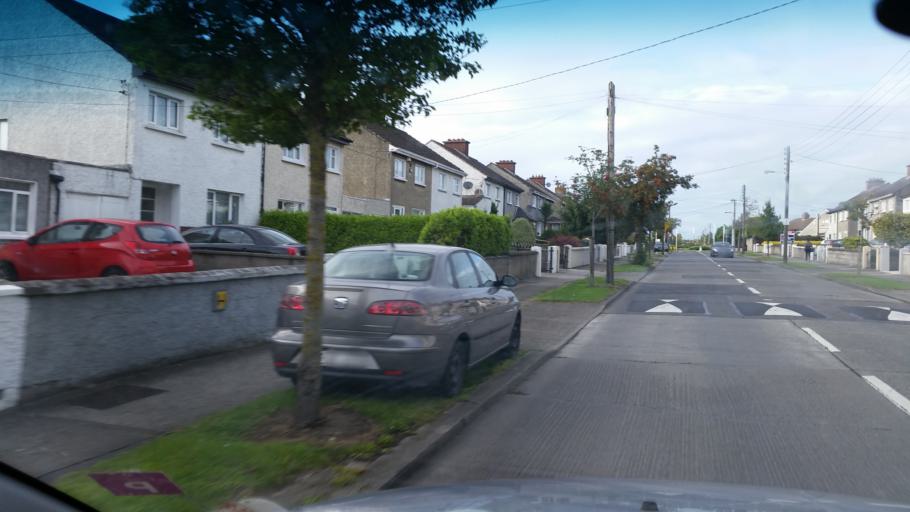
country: IE
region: Leinster
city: Ballymun
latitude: 53.3889
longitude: -6.2796
